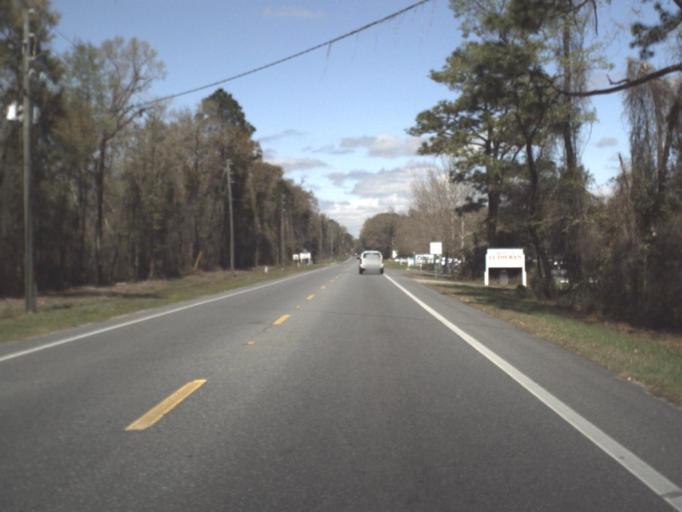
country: US
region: Florida
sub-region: Wakulla County
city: Crawfordville
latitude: 30.1079
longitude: -84.3812
